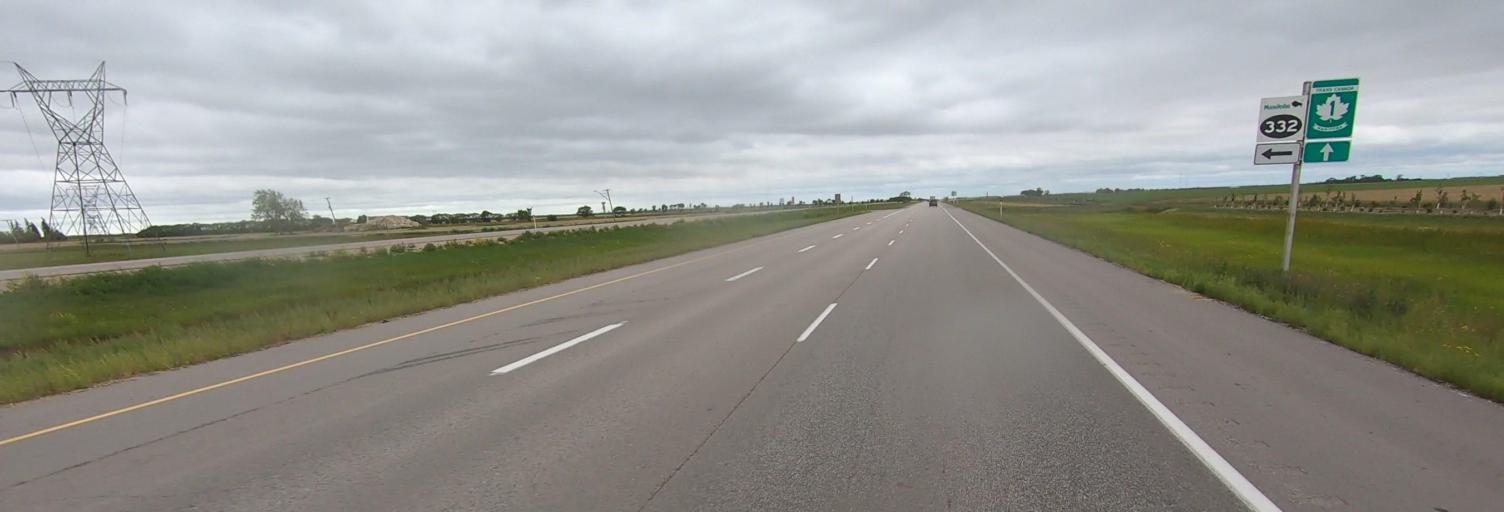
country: CA
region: Manitoba
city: Headingley
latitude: 49.8871
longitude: -97.6390
